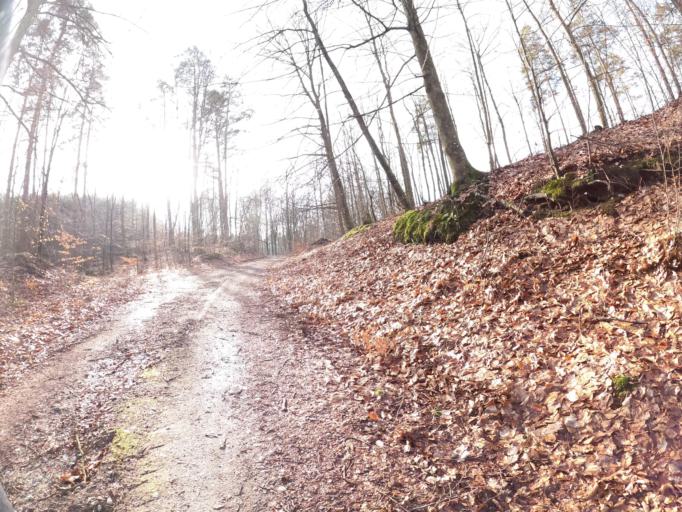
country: PL
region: West Pomeranian Voivodeship
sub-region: Powiat koszalinski
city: Polanow
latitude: 54.2258
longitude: 16.6399
